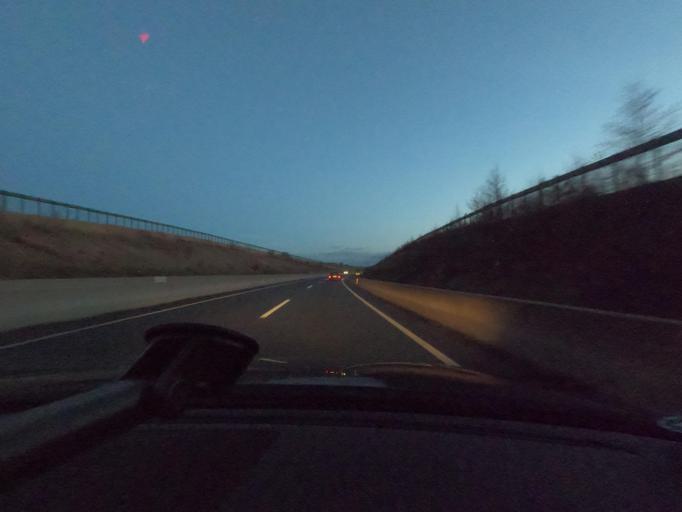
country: DE
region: Lower Saxony
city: Bad Lauterberg im Harz
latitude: 51.6054
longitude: 10.4779
